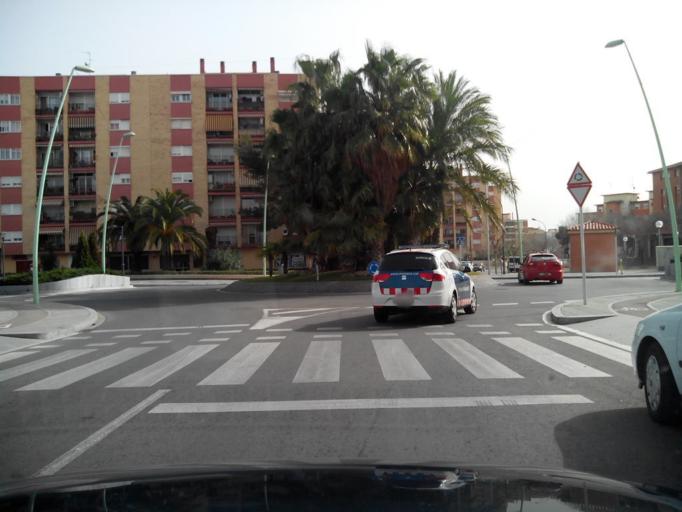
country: ES
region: Catalonia
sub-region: Provincia de Tarragona
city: Constanti
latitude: 41.1170
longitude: 1.2100
